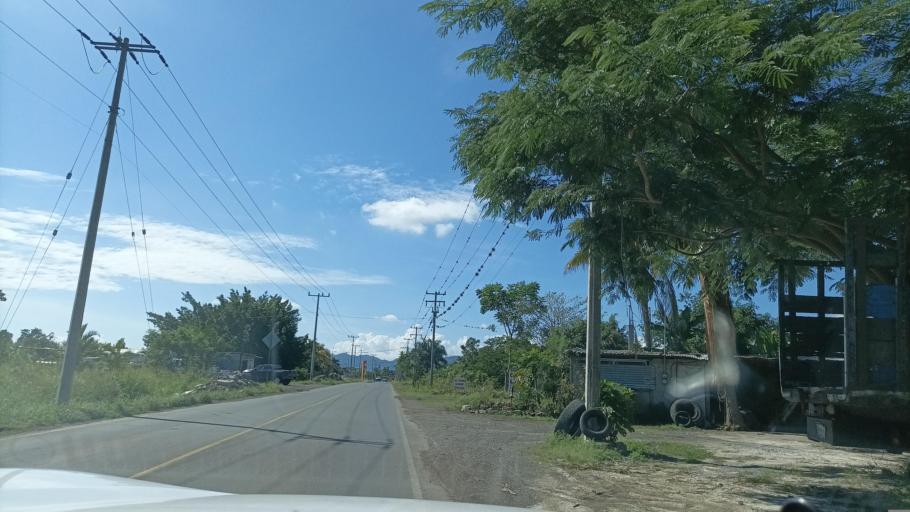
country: MX
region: Veracruz
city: Paso del Macho
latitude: 18.9675
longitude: -96.7332
